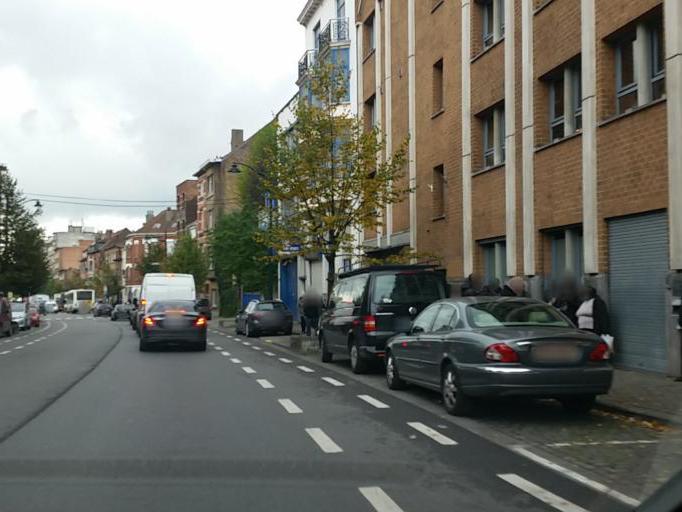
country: BE
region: Brussels Capital
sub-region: Bruxelles-Capitale
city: Brussels
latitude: 50.8381
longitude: 4.3139
